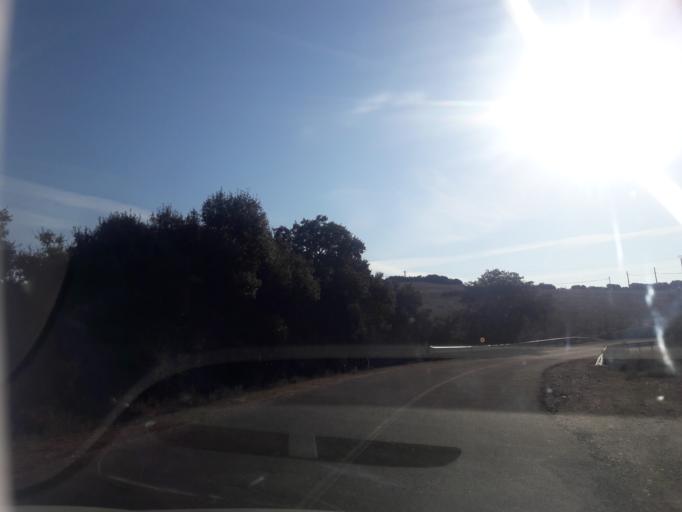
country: ES
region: Castille and Leon
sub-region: Provincia de Salamanca
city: Aldeavieja de Tormes
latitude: 40.5877
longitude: -5.6101
